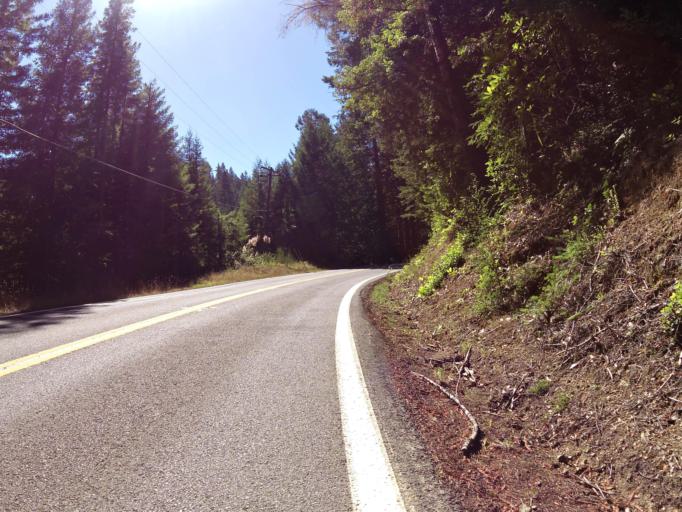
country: US
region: California
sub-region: Mendocino County
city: Fort Bragg
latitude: 39.7309
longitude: -123.8114
